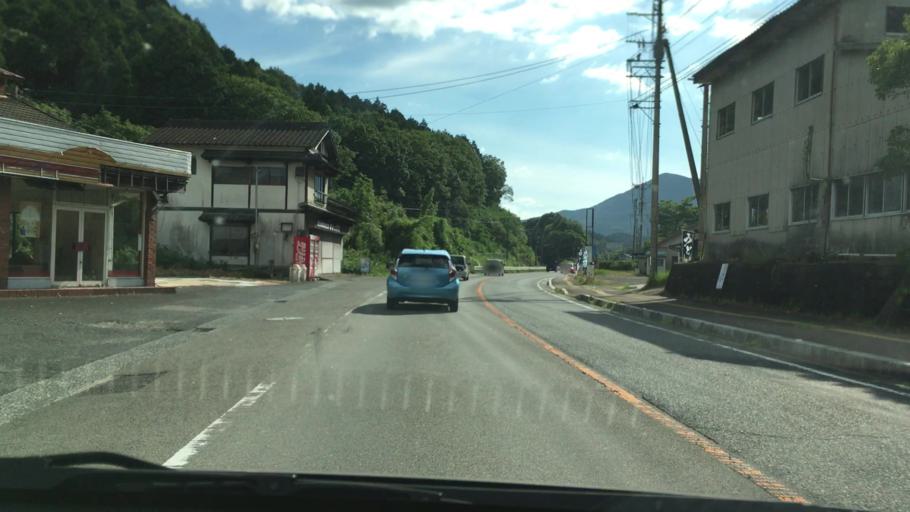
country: JP
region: Saga Prefecture
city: Imaricho-ko
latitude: 33.1878
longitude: 129.8588
